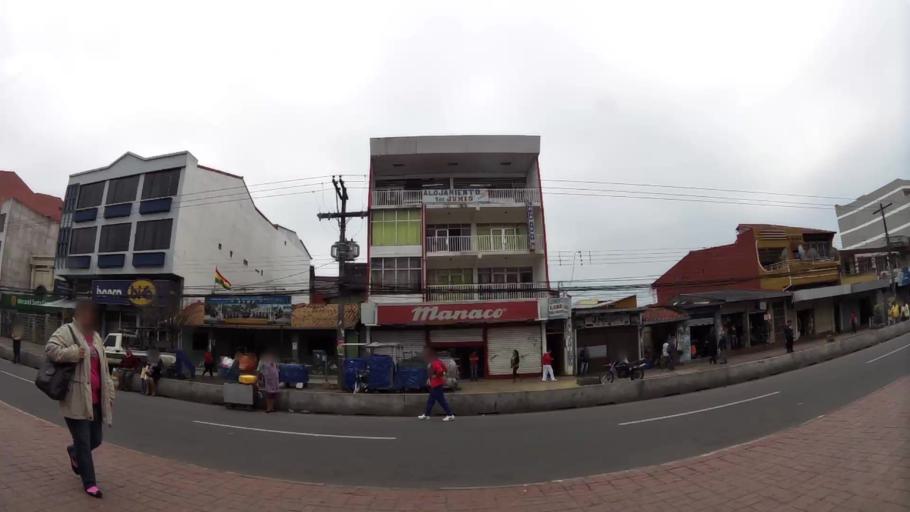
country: BO
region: Santa Cruz
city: Santa Cruz de la Sierra
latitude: -17.7966
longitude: -63.1911
